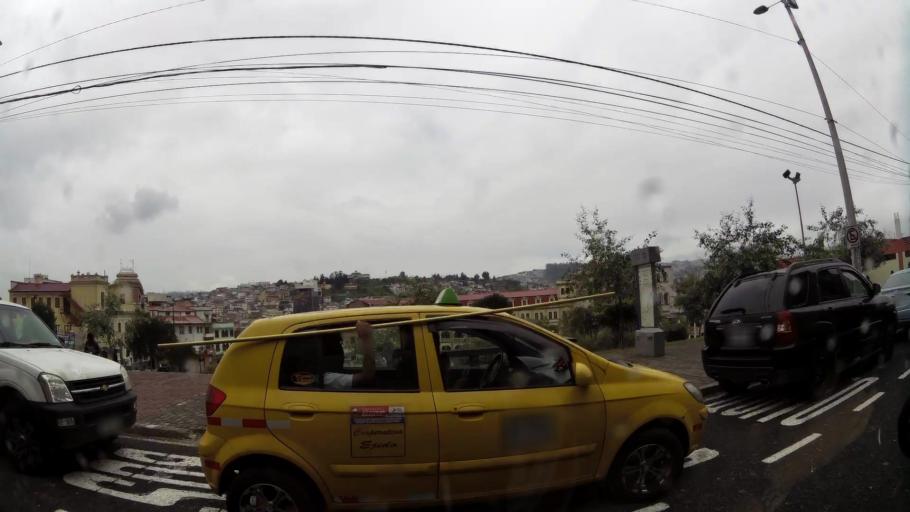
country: EC
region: Pichincha
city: Quito
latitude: -0.2151
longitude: -78.5072
